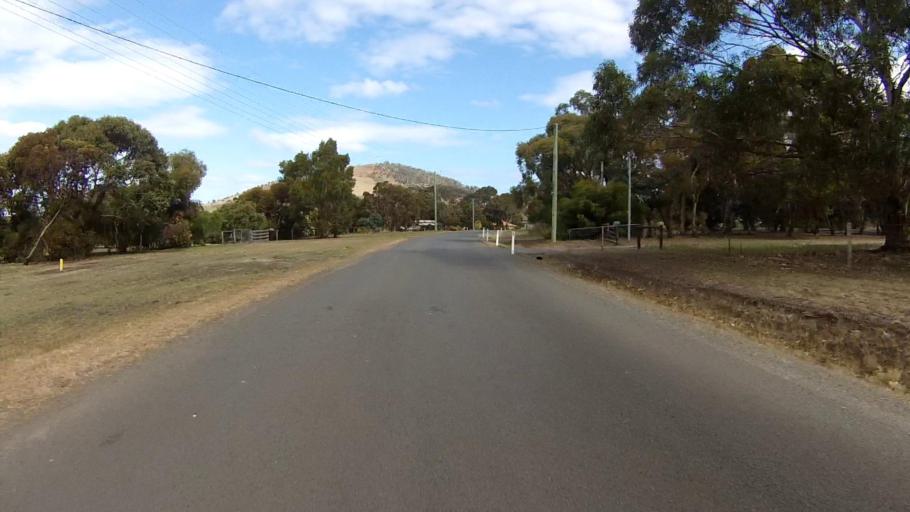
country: AU
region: Tasmania
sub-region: Clarence
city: Acton Park
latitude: -42.8607
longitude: 147.4854
